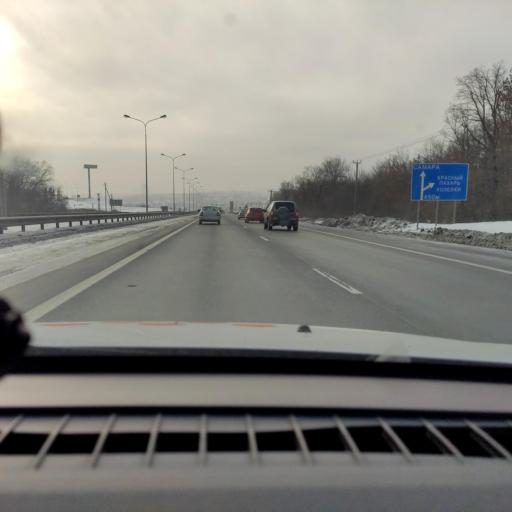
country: RU
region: Samara
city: Novosemeykino
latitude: 53.3295
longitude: 50.3000
